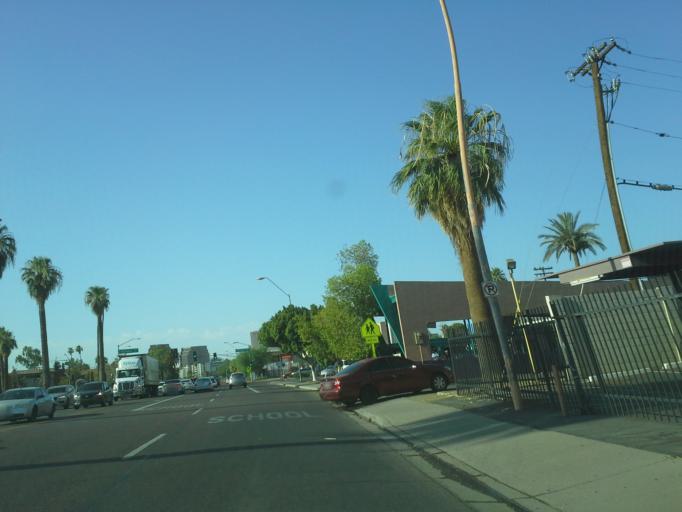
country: US
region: Arizona
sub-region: Maricopa County
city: Phoenix
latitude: 33.4670
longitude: -112.0695
